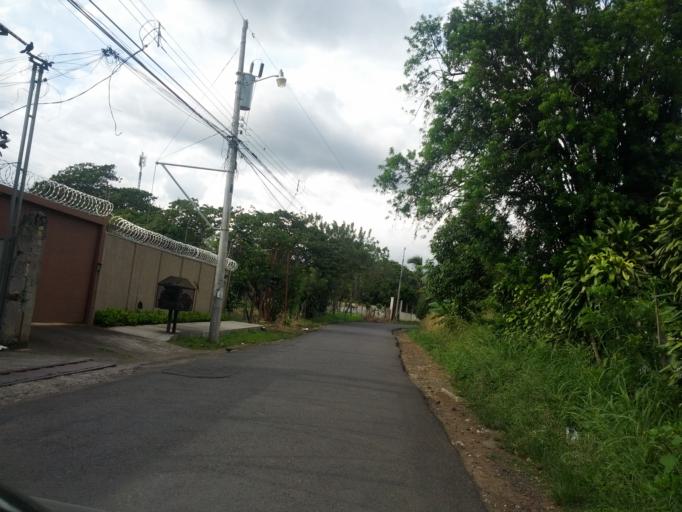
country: CR
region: Heredia
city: Llorente
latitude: 10.0210
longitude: -84.1758
